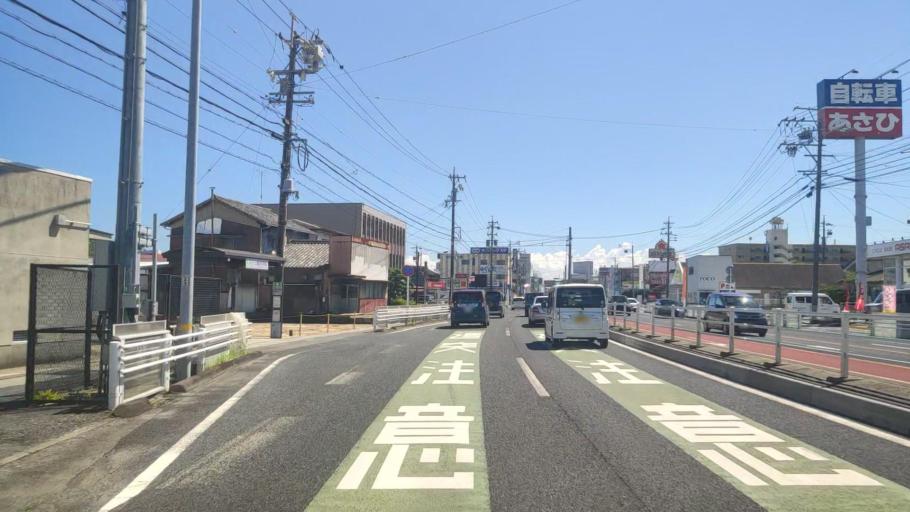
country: JP
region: Mie
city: Tsu-shi
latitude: 34.7469
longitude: 136.5206
